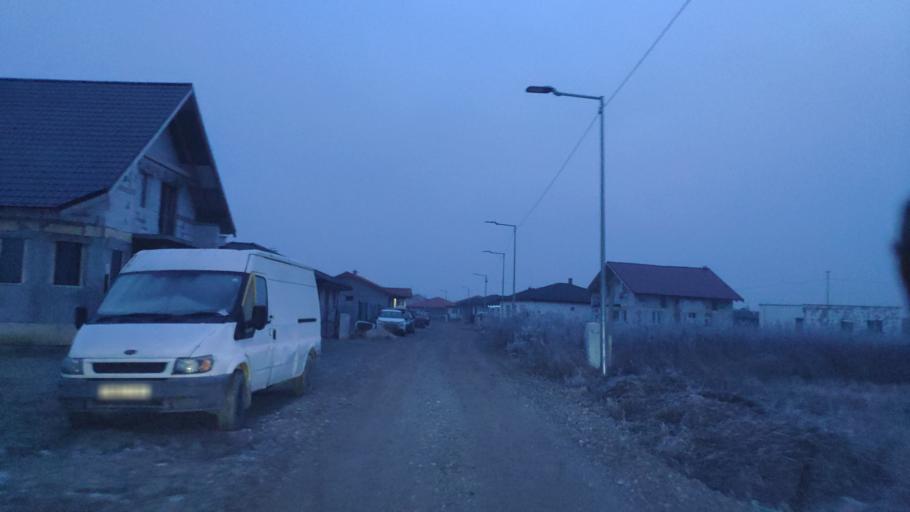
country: SK
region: Kosicky
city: Kosice
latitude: 48.6155
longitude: 21.3323
